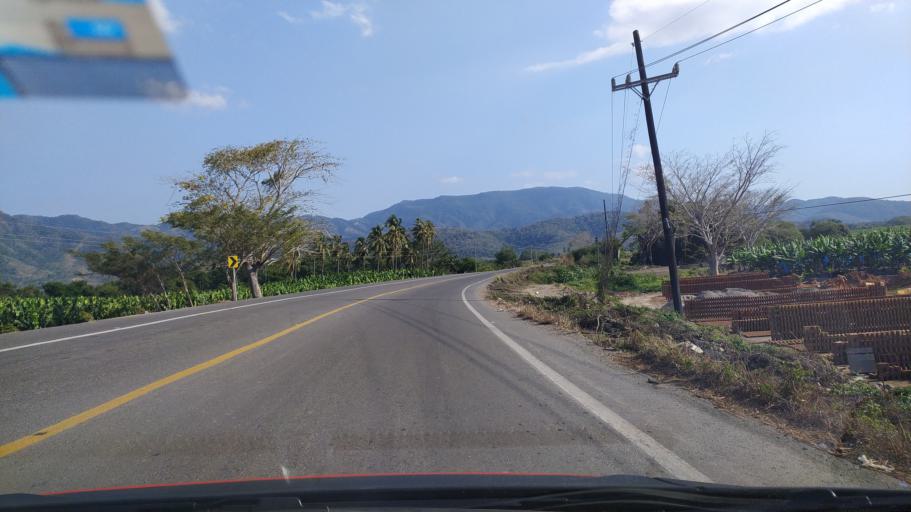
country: MX
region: Michoacan
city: Coahuayana Viejo
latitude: 18.6713
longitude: -103.6735
